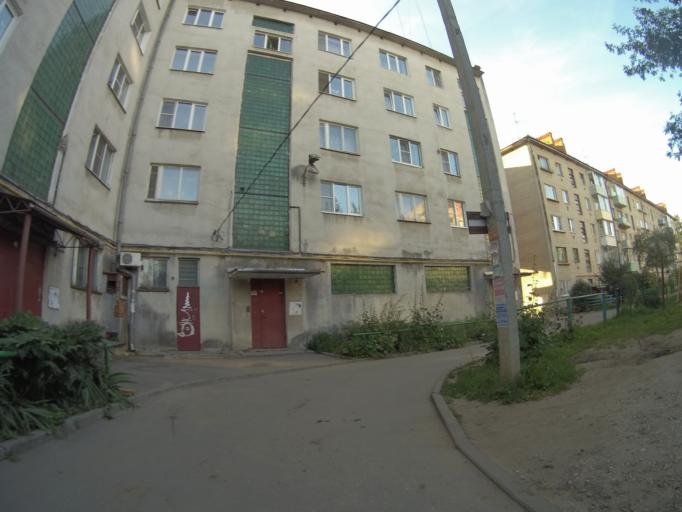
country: RU
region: Vladimir
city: Vladimir
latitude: 56.1500
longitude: 40.3752
